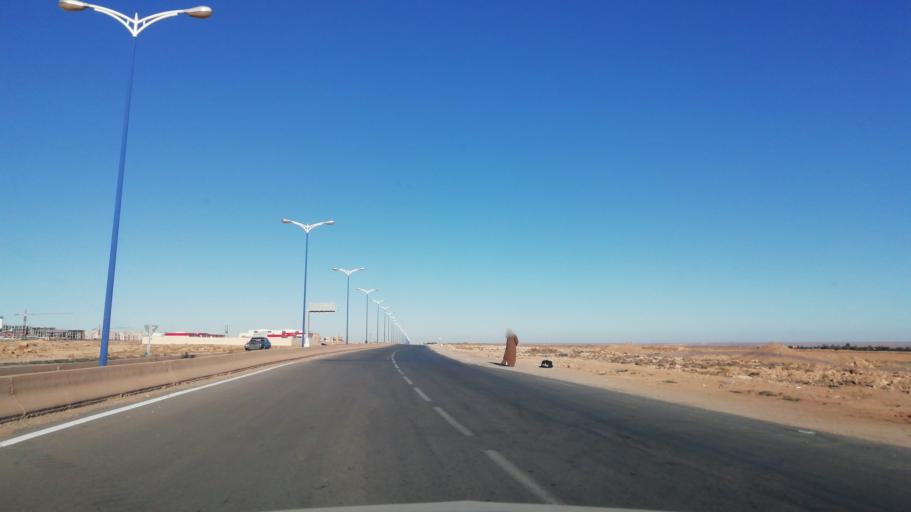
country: DZ
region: Wilaya de Naama
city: Naama
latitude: 33.5422
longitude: -0.2533
